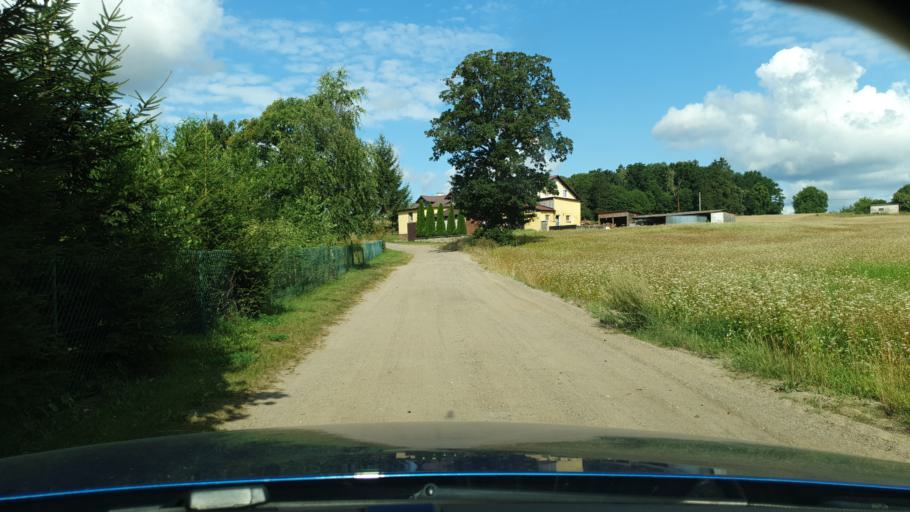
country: PL
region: Pomeranian Voivodeship
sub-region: Powiat czluchowski
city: Przechlewo
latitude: 53.8056
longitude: 17.3510
